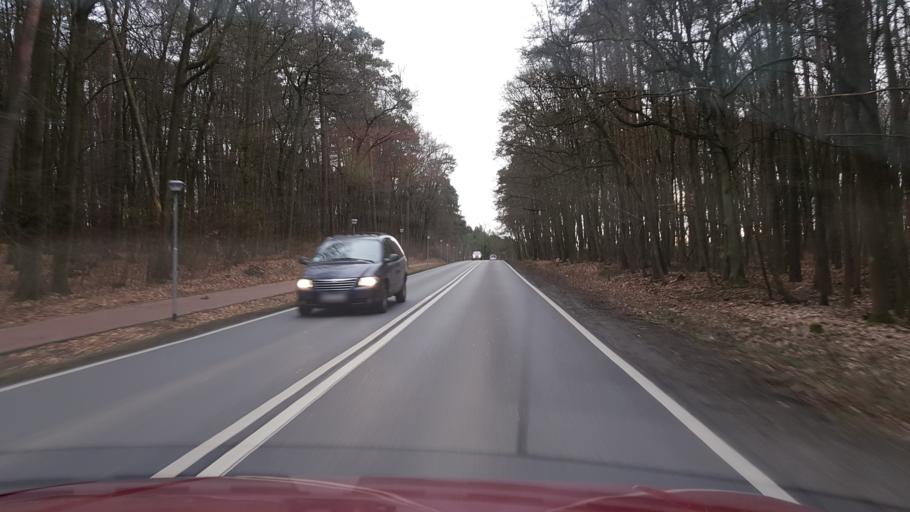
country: PL
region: West Pomeranian Voivodeship
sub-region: Szczecin
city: Szczecin
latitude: 53.4817
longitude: 14.4839
